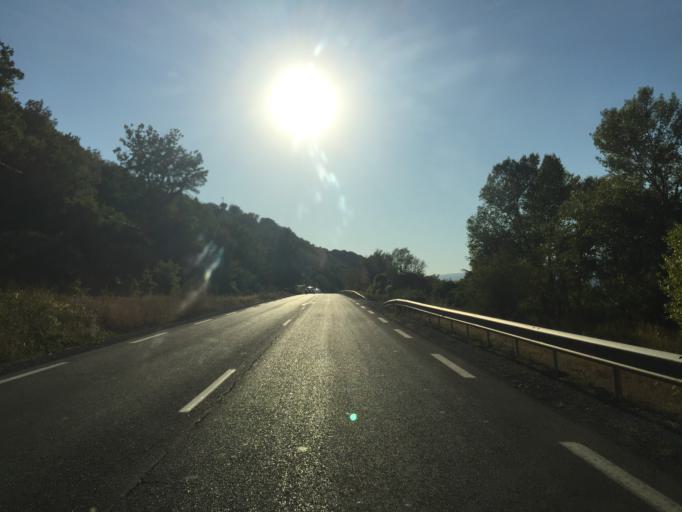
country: FR
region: Provence-Alpes-Cote d'Azur
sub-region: Departement des Alpes-de-Haute-Provence
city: Malijai
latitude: 44.0422
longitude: 6.0366
